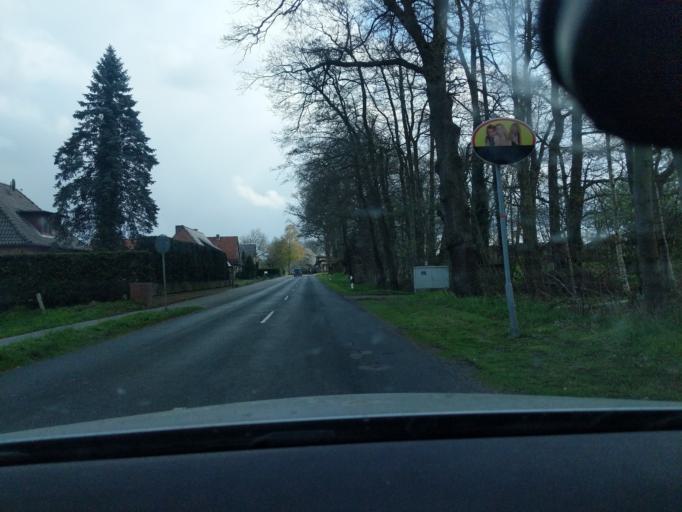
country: DE
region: Lower Saxony
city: Deinste
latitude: 53.5257
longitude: 9.4850
